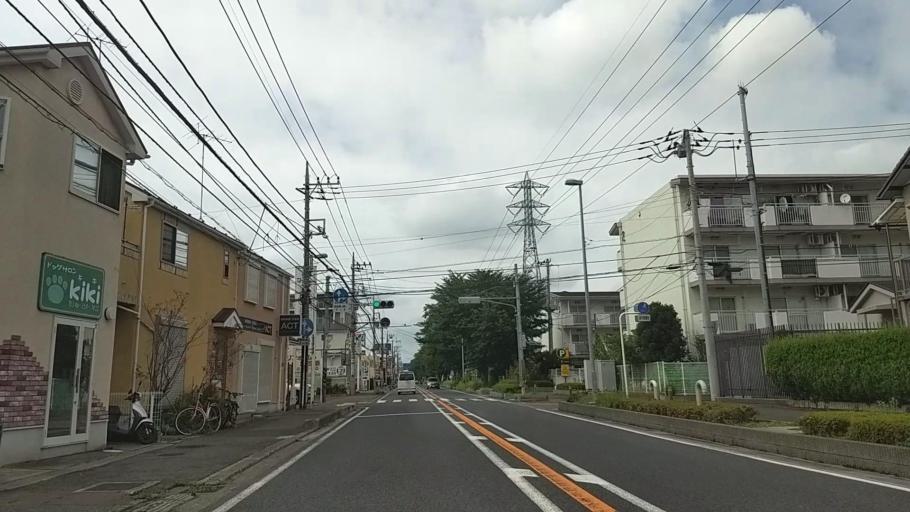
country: JP
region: Kanagawa
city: Minami-rinkan
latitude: 35.4438
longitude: 139.4672
